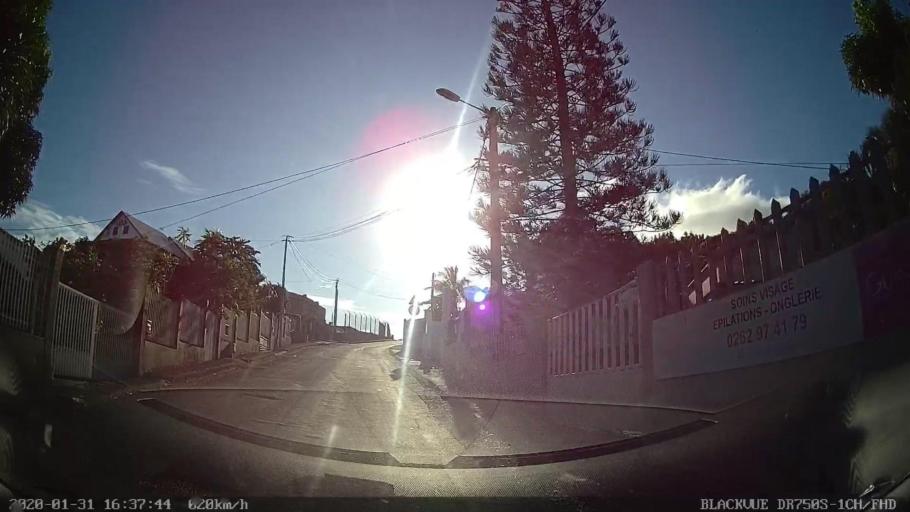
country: RE
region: Reunion
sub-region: Reunion
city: Saint-Denis
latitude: -20.9065
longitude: 55.4860
